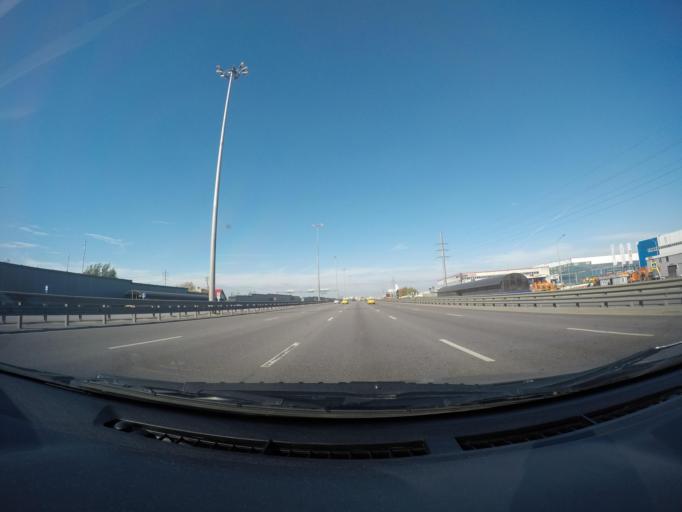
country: RU
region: Moskovskaya
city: Tomilino
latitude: 55.6431
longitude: 37.9172
